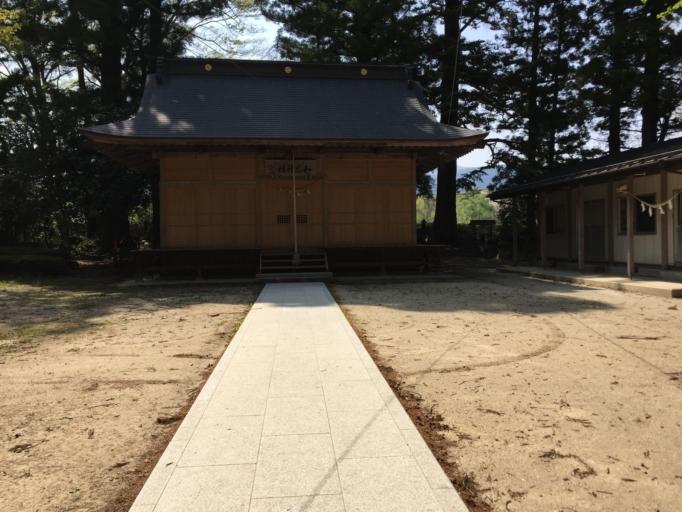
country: JP
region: Fukushima
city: Fukushima-shi
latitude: 37.7302
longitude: 140.3774
